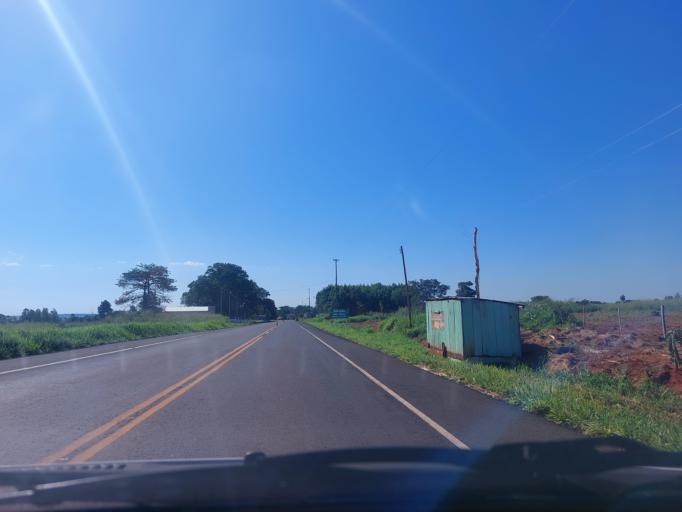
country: PY
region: San Pedro
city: Guayaybi
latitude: -24.3163
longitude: -56.1652
